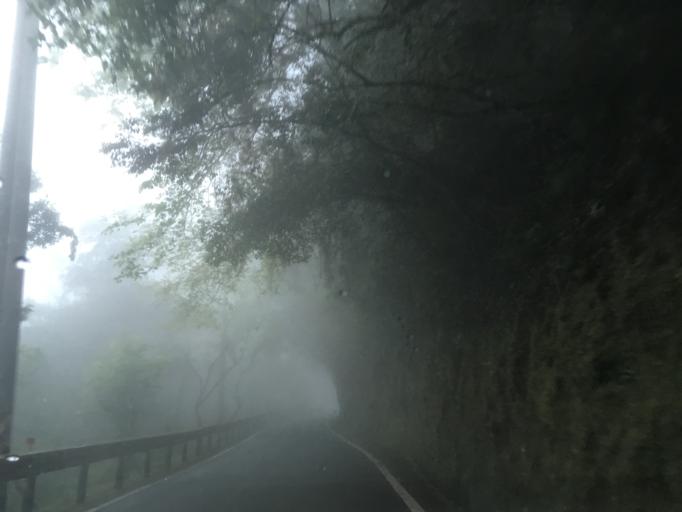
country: TW
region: Taiwan
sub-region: Hualien
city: Hualian
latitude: 24.1935
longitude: 121.4172
